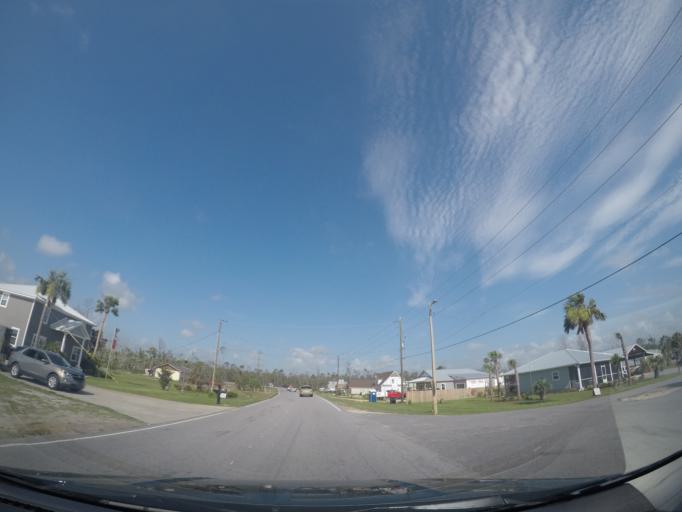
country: US
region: Florida
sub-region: Bay County
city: Mexico Beach
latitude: 29.9409
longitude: -85.3912
